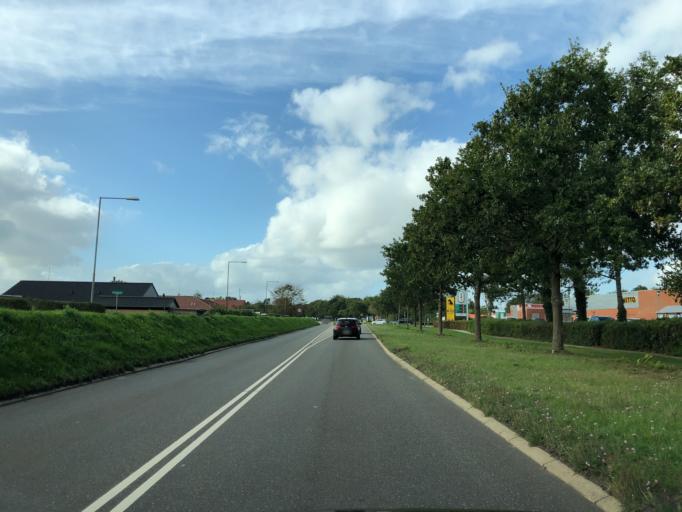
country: DK
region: Central Jutland
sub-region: Holstebro Kommune
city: Holstebro
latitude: 56.3628
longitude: 8.5948
